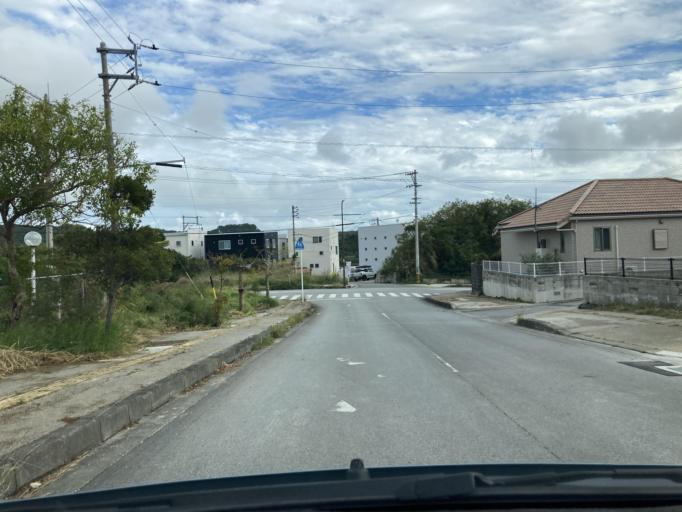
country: JP
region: Okinawa
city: Tomigusuku
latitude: 26.1753
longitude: 127.7445
